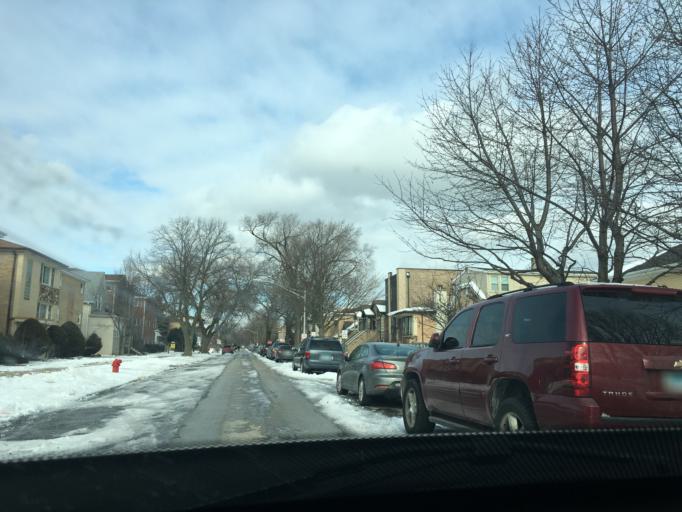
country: US
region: Illinois
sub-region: Cook County
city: Elmwood Park
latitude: 41.9296
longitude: -87.8126
